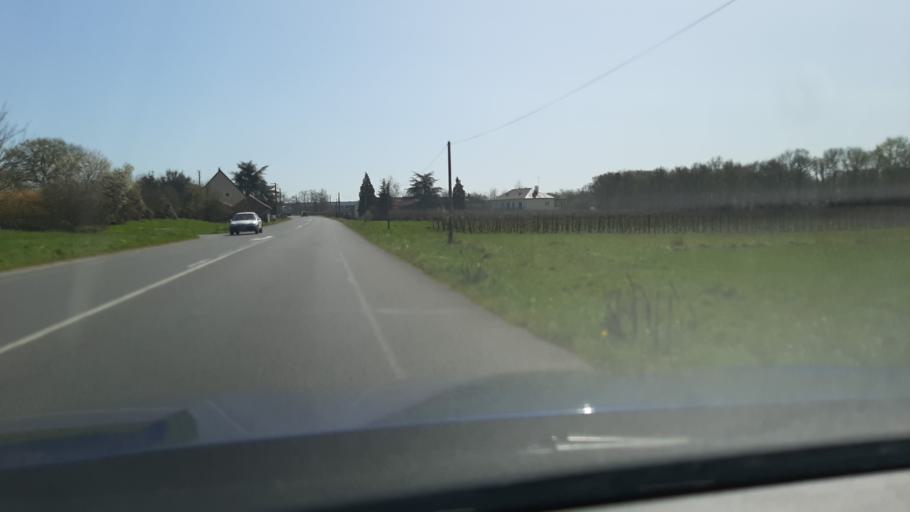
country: FR
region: Pays de la Loire
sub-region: Departement de Maine-et-Loire
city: Ecouflant
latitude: 47.5235
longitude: -0.4991
